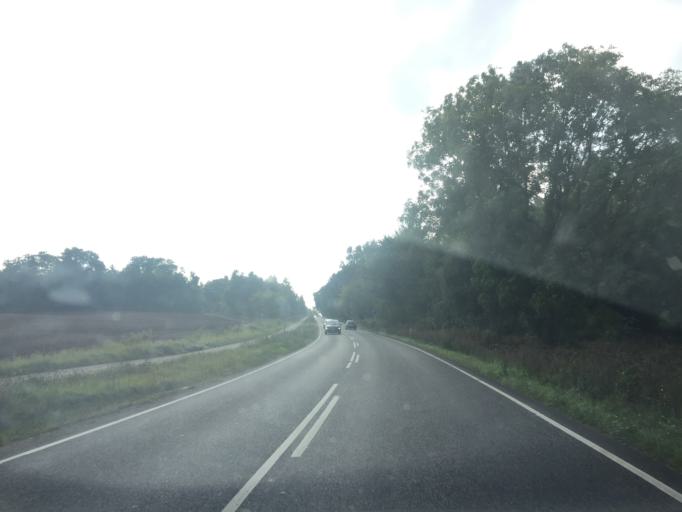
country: DK
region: Zealand
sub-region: Lejre Kommune
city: Ejby
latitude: 55.6699
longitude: 11.8275
